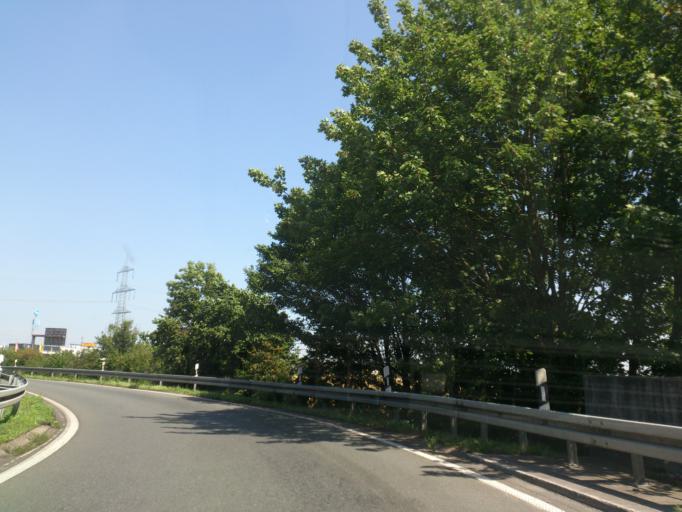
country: DE
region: North Rhine-Westphalia
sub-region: Regierungsbezirk Detmold
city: Paderborn
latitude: 51.6815
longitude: 8.7141
